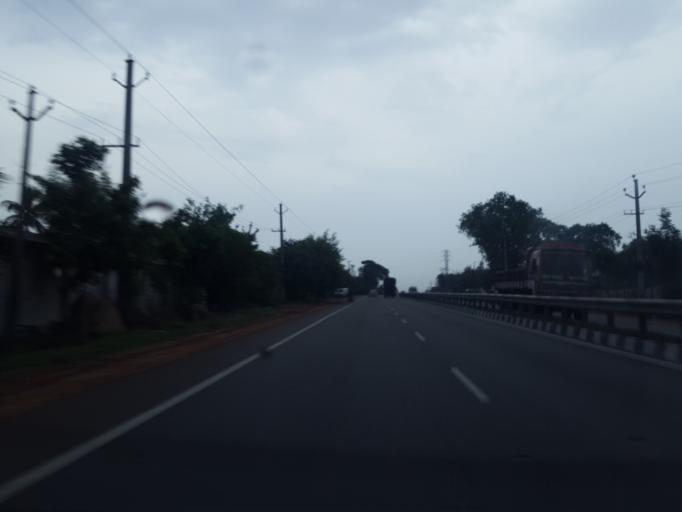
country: IN
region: Telangana
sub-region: Rangareddi
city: Sriramnagar
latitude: 17.1605
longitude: 78.2954
